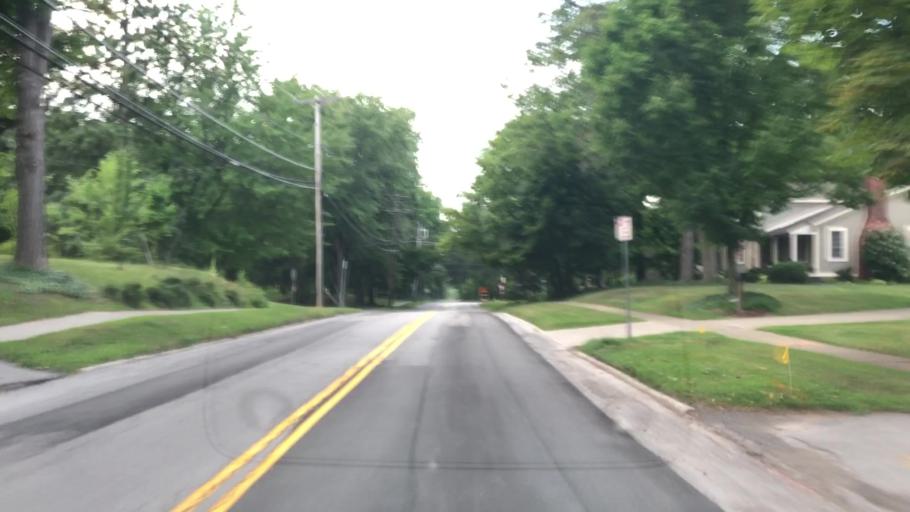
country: US
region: New York
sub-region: Erie County
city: East Aurora
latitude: 42.7719
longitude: -78.6079
